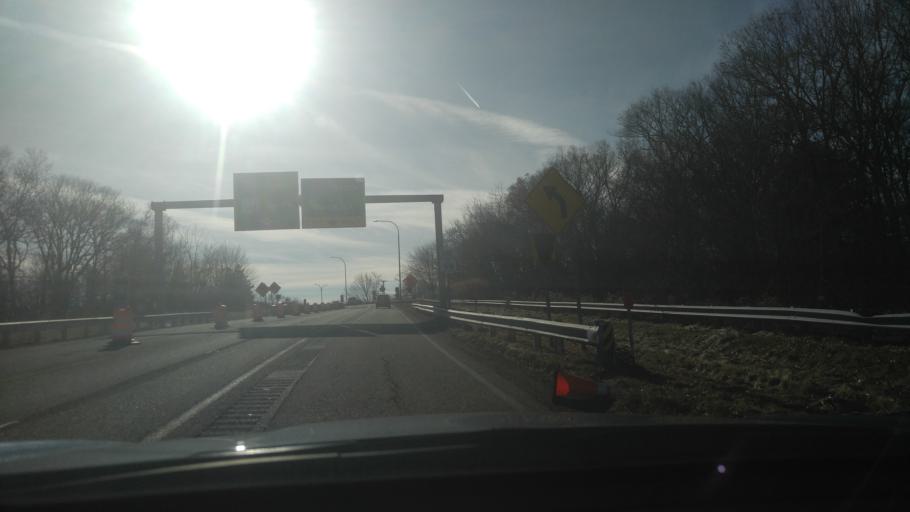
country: US
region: Rhode Island
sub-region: Providence County
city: Cumberland Hill
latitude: 41.9528
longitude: -71.4839
